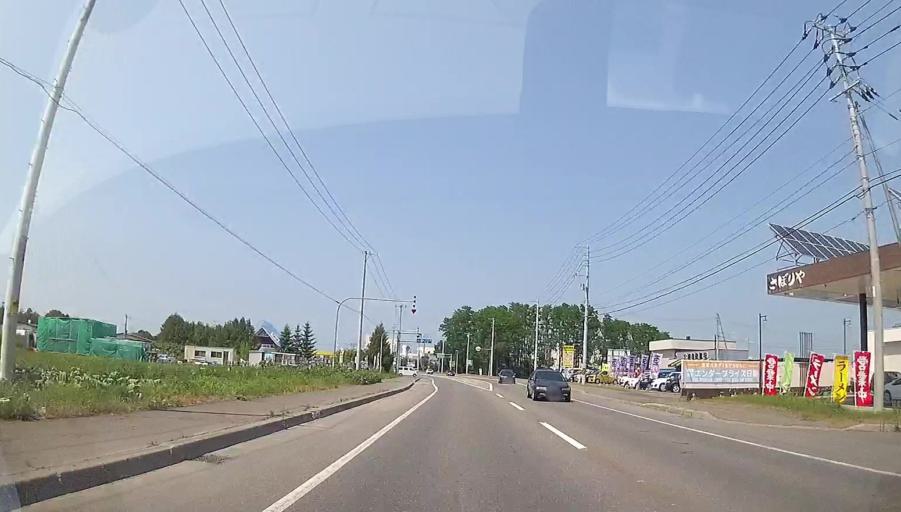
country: JP
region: Hokkaido
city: Otofuke
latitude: 42.9750
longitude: 143.2080
